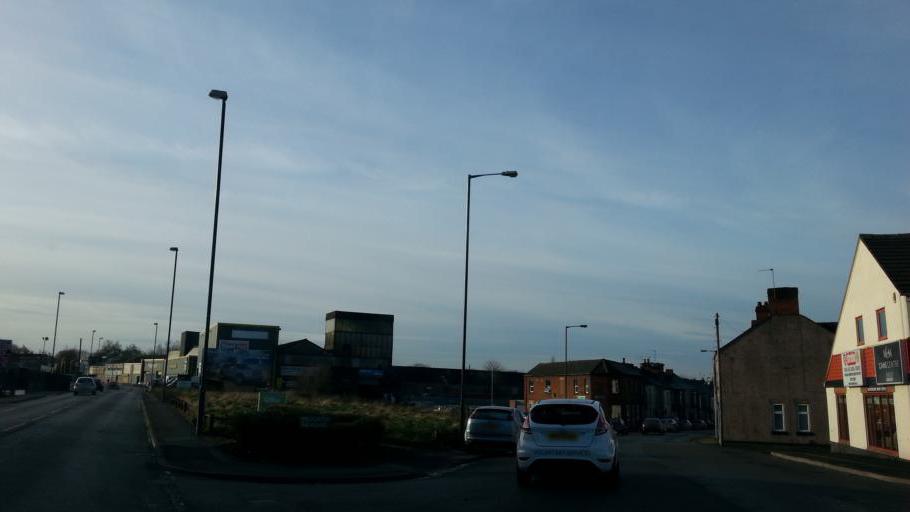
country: GB
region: England
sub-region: Stoke-on-Trent
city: Stoke-on-Trent
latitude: 53.0401
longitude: -2.1810
